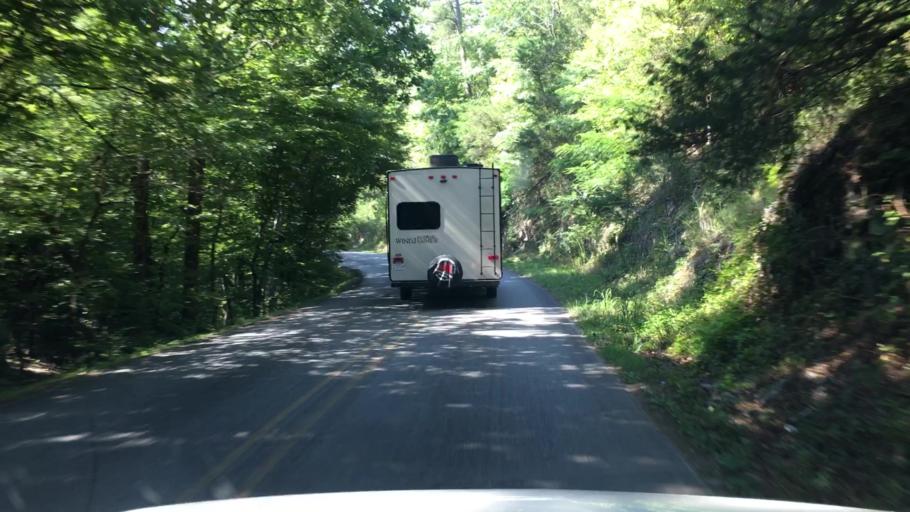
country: US
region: Arkansas
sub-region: Garland County
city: Piney
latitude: 34.5276
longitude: -93.3356
